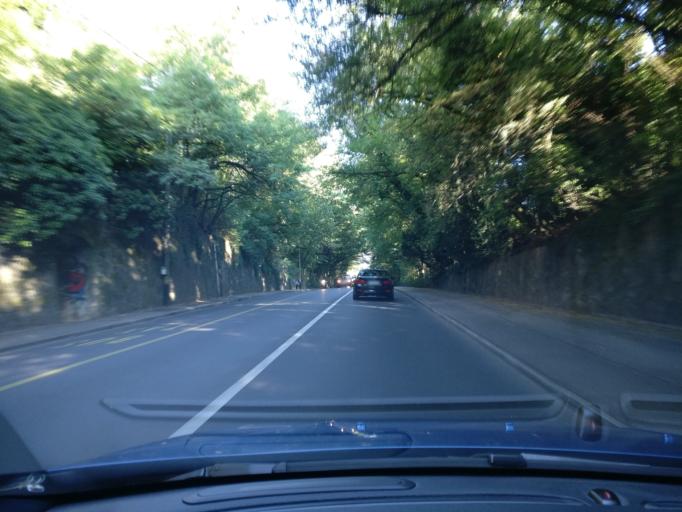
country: CH
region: Geneva
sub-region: Geneva
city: Le Grand-Saconnex
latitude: 46.2272
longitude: 6.1299
